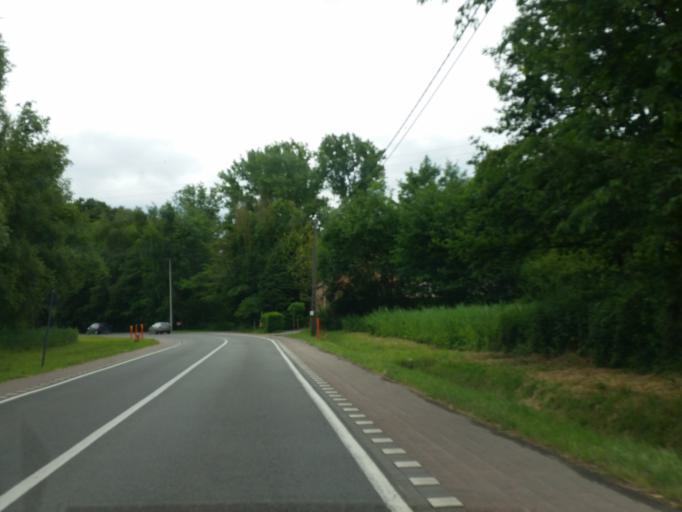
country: BE
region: Flanders
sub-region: Provincie Antwerpen
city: Ranst
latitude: 51.2000
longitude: 4.5984
